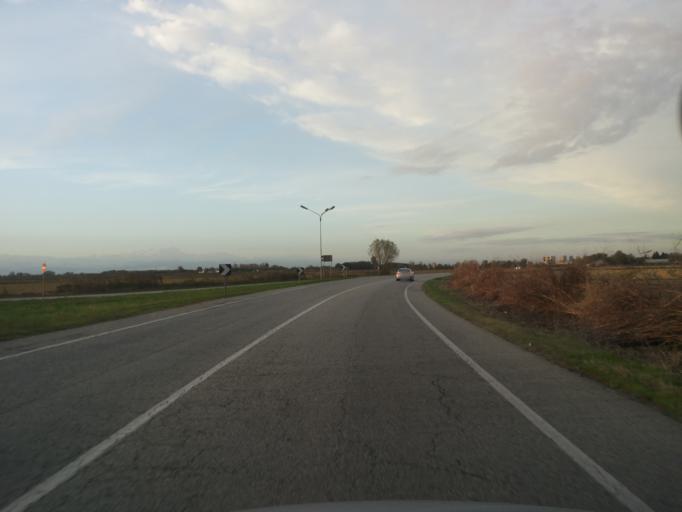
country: IT
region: Piedmont
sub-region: Provincia di Vercelli
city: Stroppiana
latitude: 45.2384
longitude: 8.4575
